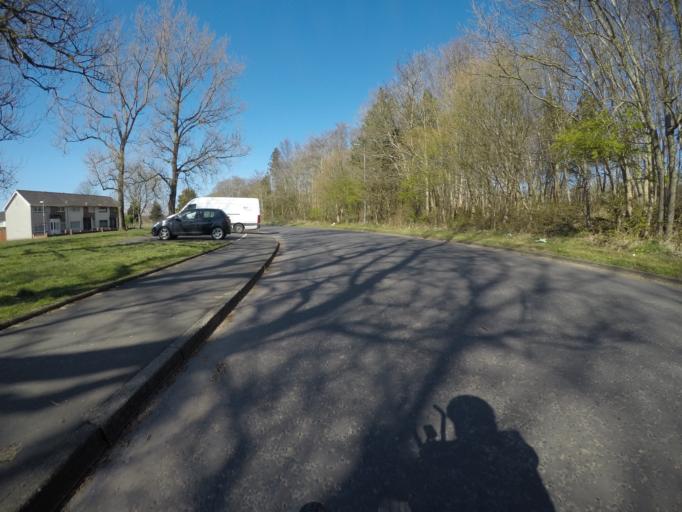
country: GB
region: Scotland
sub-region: North Ayrshire
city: Irvine
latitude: 55.6353
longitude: -4.6615
